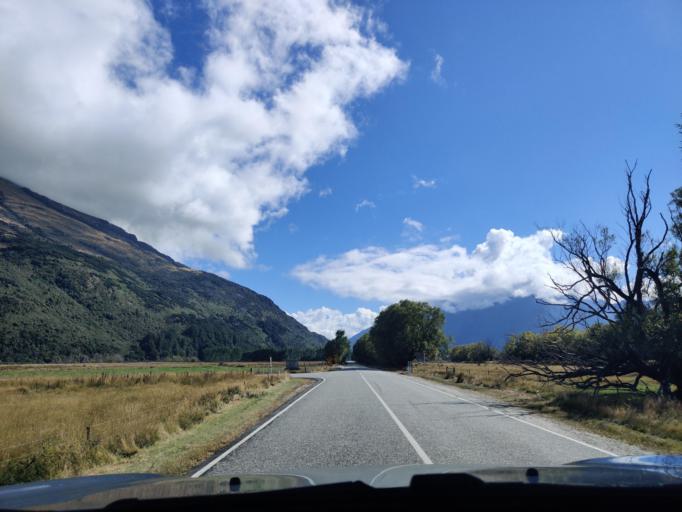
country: NZ
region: Otago
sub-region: Queenstown-Lakes District
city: Queenstown
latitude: -44.7836
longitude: 168.3946
